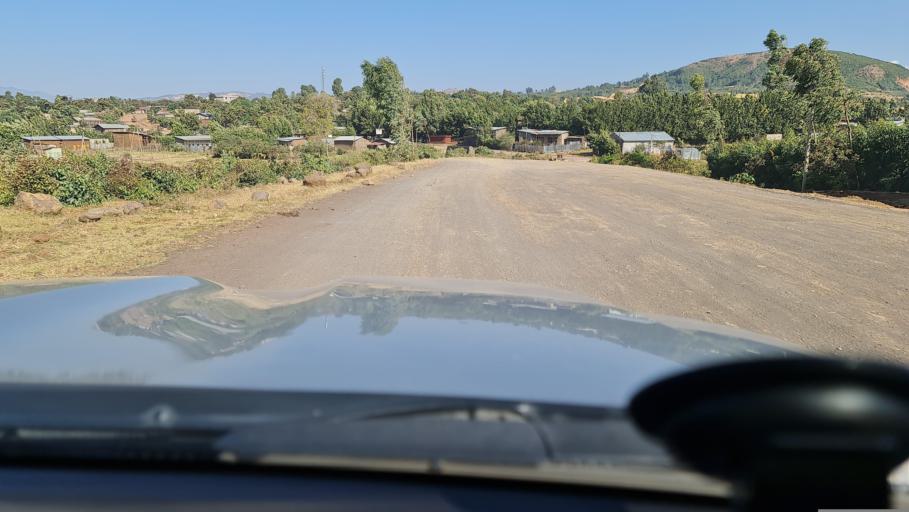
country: ET
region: Oromiya
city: Waliso
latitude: 8.6031
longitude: 37.9276
